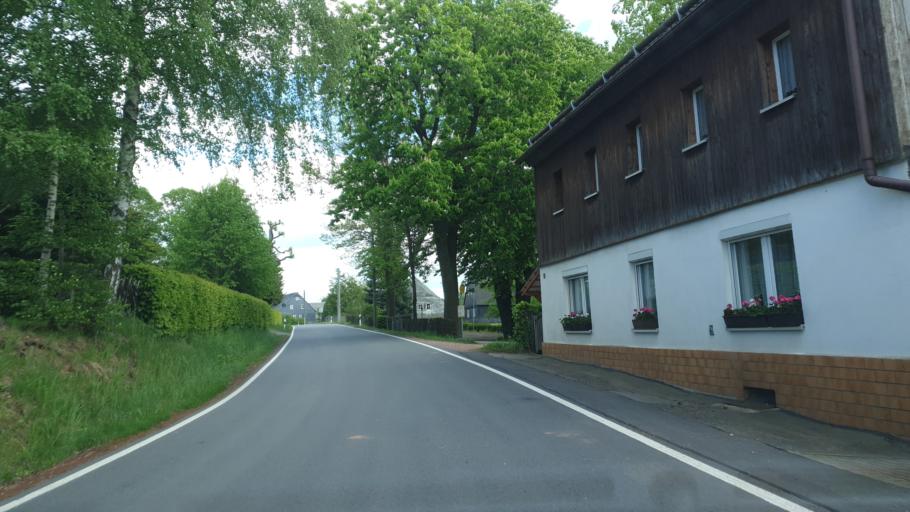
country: DE
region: Saxony
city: Kirchberg
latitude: 50.7801
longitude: 12.7748
